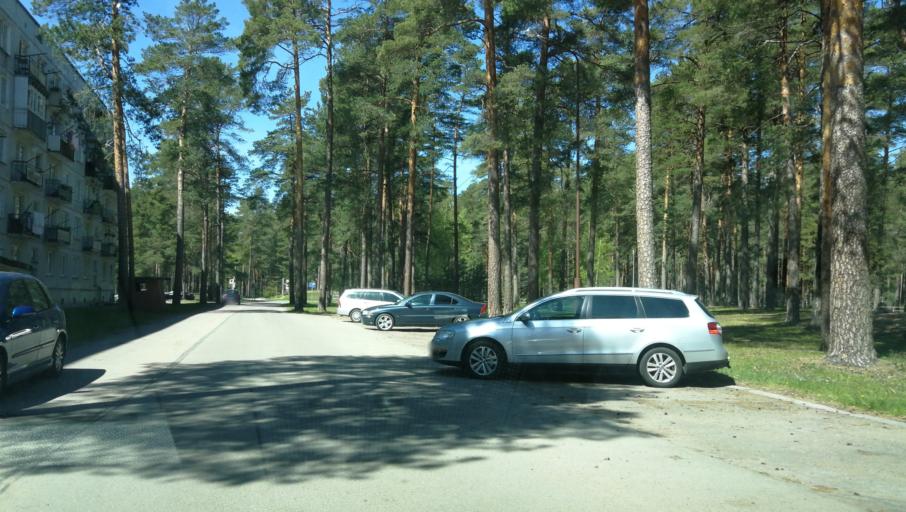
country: LV
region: Adazi
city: Adazi
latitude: 57.0916
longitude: 24.3613
